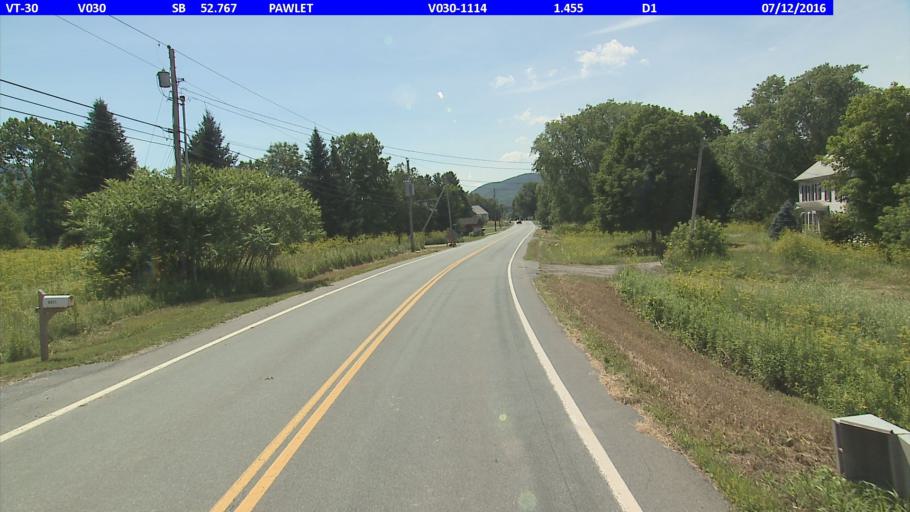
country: US
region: New York
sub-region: Washington County
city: Granville
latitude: 43.3313
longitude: -73.1749
